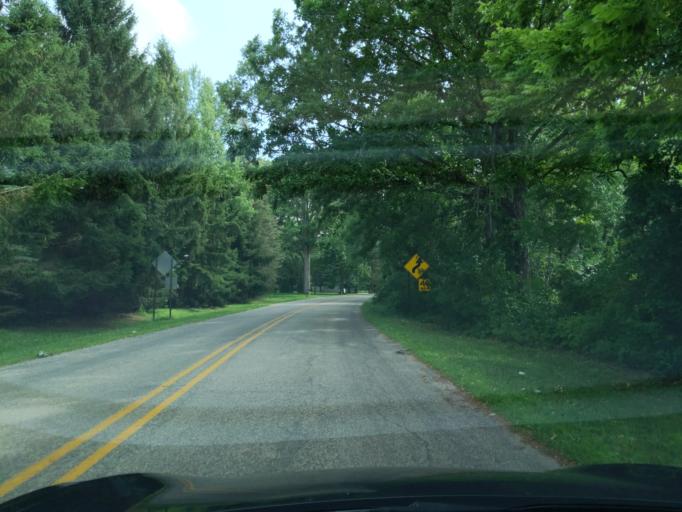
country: US
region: Michigan
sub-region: Eaton County
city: Dimondale
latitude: 42.5793
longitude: -84.6012
